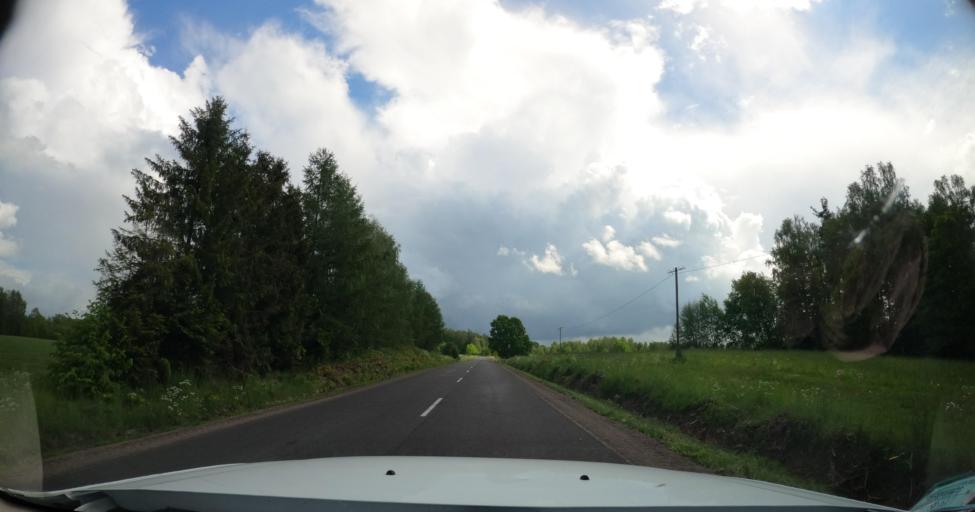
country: PL
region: Pomeranian Voivodeship
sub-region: Powiat bytowski
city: Czarna Dabrowka
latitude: 54.3513
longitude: 17.5781
